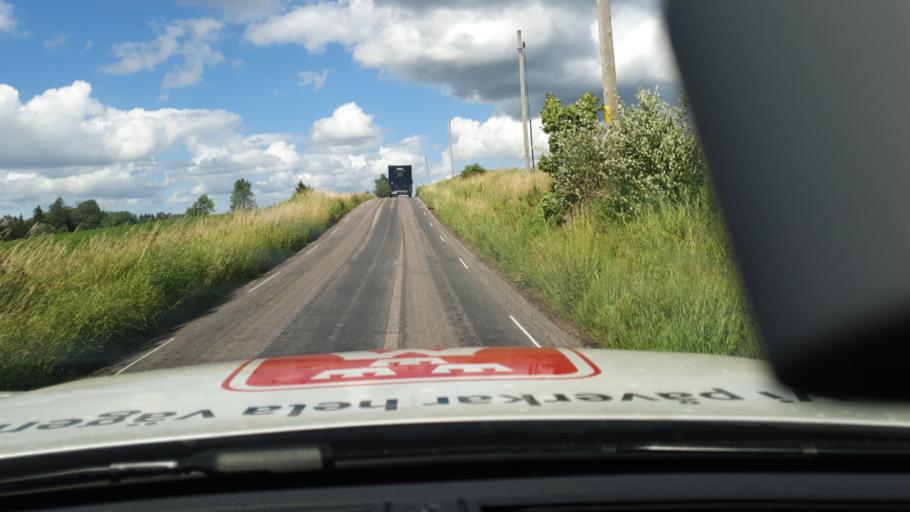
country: SE
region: Vaestra Goetaland
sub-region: Skara Kommun
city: Axvall
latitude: 58.4002
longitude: 13.6608
